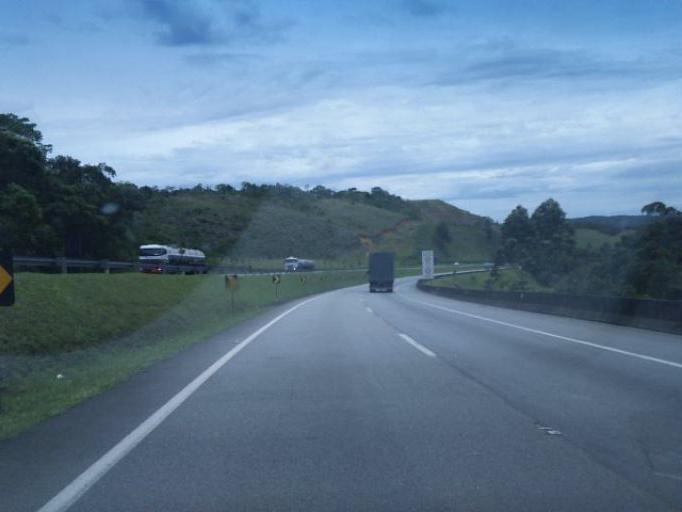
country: BR
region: Sao Paulo
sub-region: Juquitiba
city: Juquitiba
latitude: -23.9932
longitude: -47.1475
